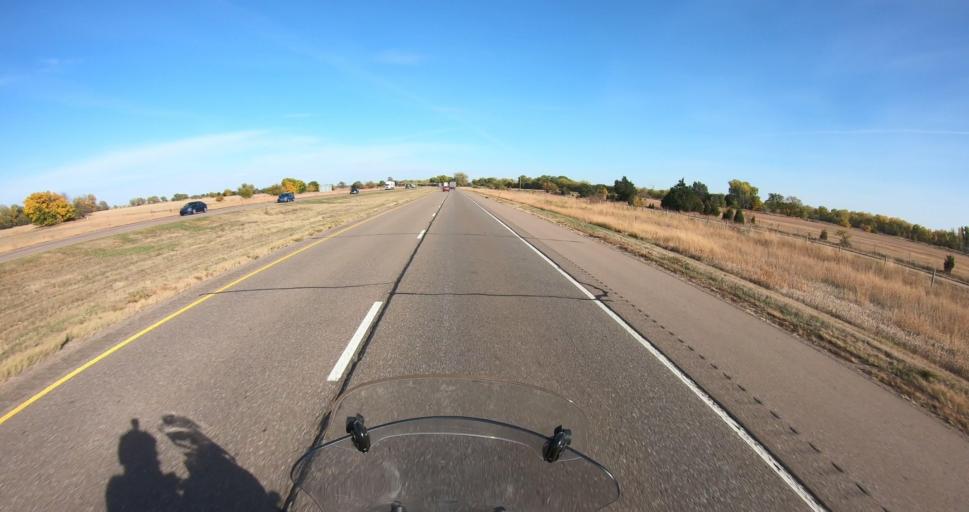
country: US
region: Nebraska
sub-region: Buffalo County
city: Shelton
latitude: 40.7223
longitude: -98.7132
